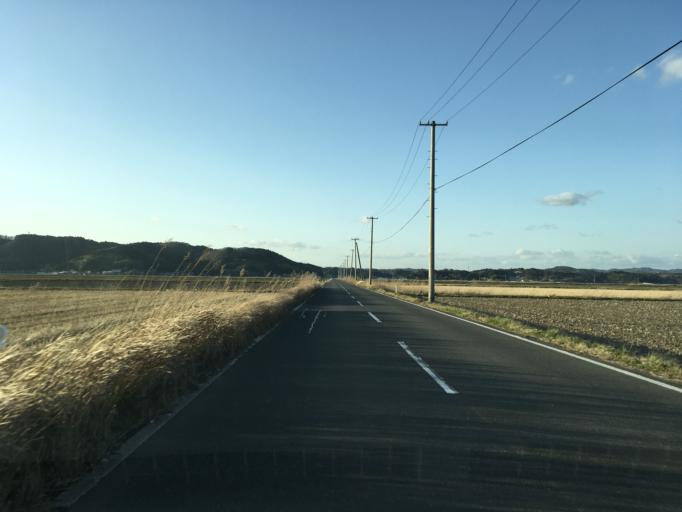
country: JP
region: Iwate
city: Ichinoseki
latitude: 38.7396
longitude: 141.2383
